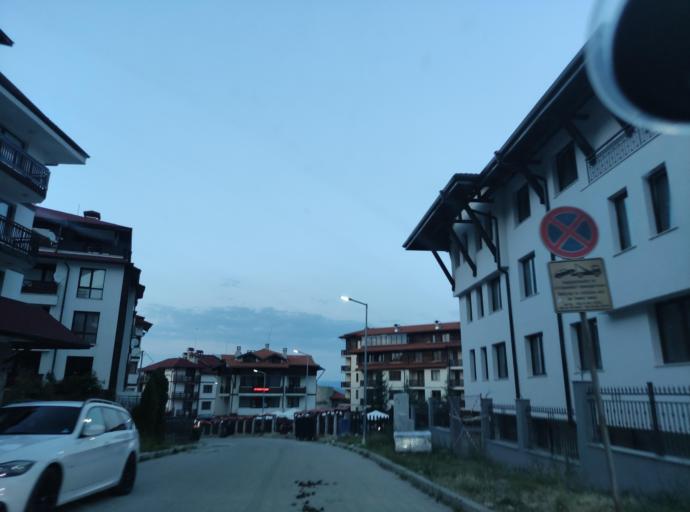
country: BG
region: Blagoevgrad
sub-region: Obshtina Bansko
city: Bansko
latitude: 41.8266
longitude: 23.4813
